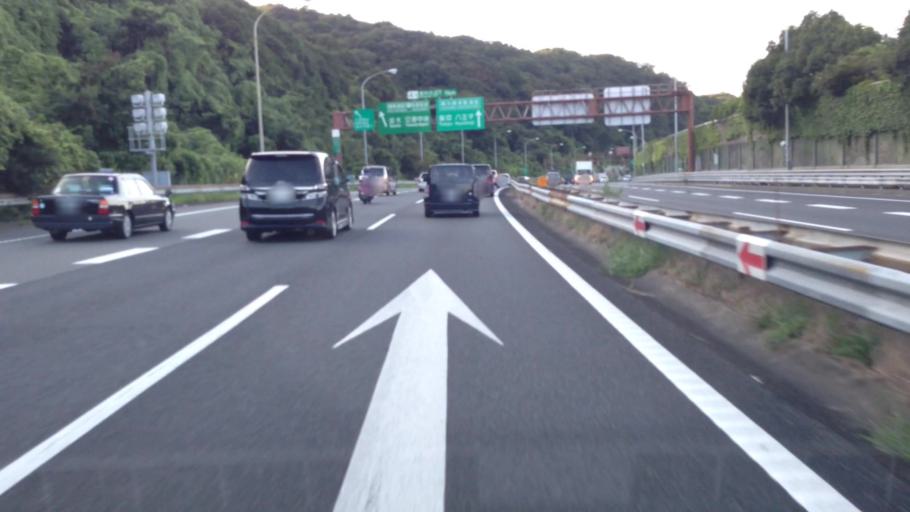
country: JP
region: Kanagawa
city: Zushi
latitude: 35.3378
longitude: 139.5907
